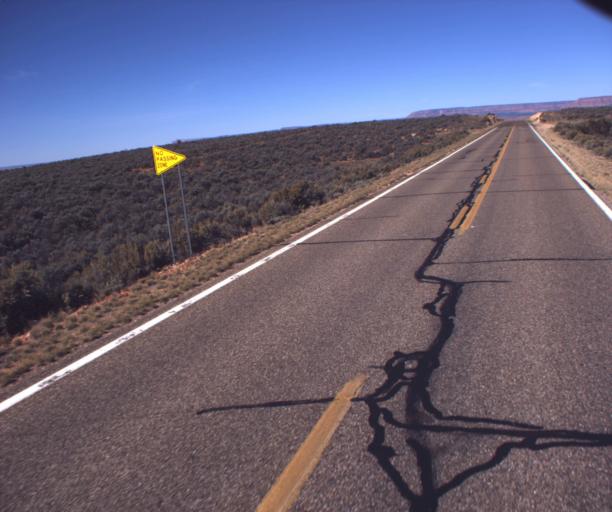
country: US
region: Arizona
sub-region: Coconino County
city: Fredonia
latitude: 36.8945
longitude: -112.3626
